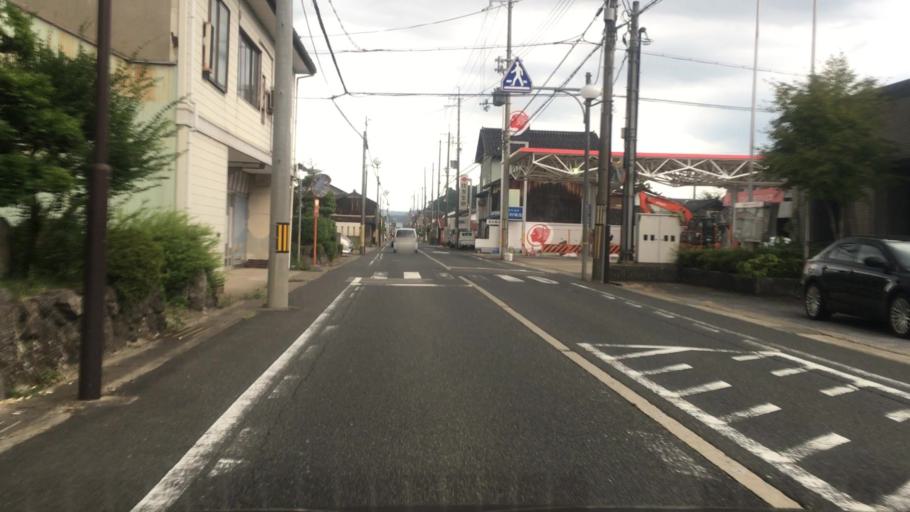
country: JP
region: Hyogo
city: Toyooka
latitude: 35.4710
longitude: 134.7795
